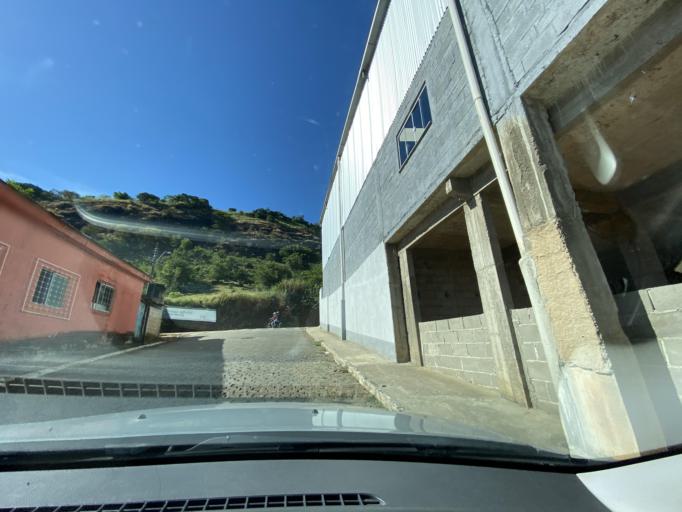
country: BR
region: Espirito Santo
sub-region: Jeronimo Monteiro
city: Jeronimo Monteiro
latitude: -20.7936
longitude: -41.3979
